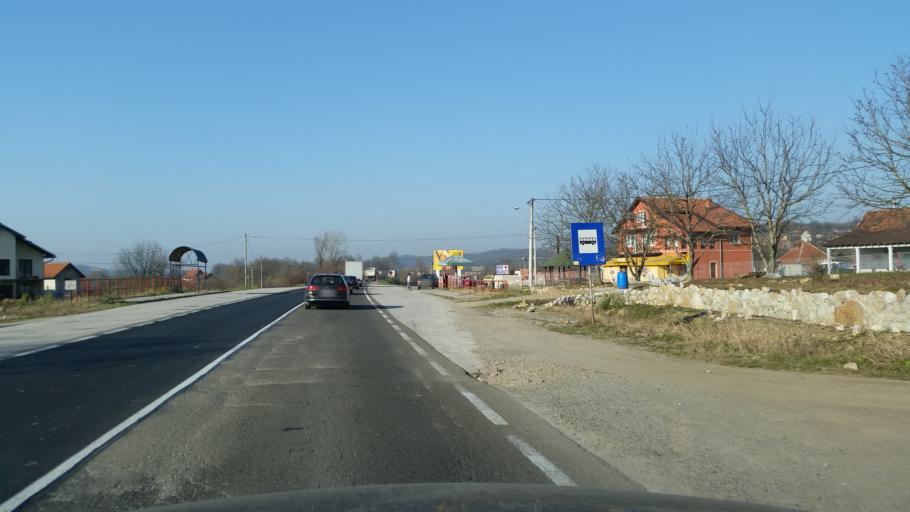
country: RS
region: Central Serbia
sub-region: Belgrade
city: Lazarevac
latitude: 44.3215
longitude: 20.2263
